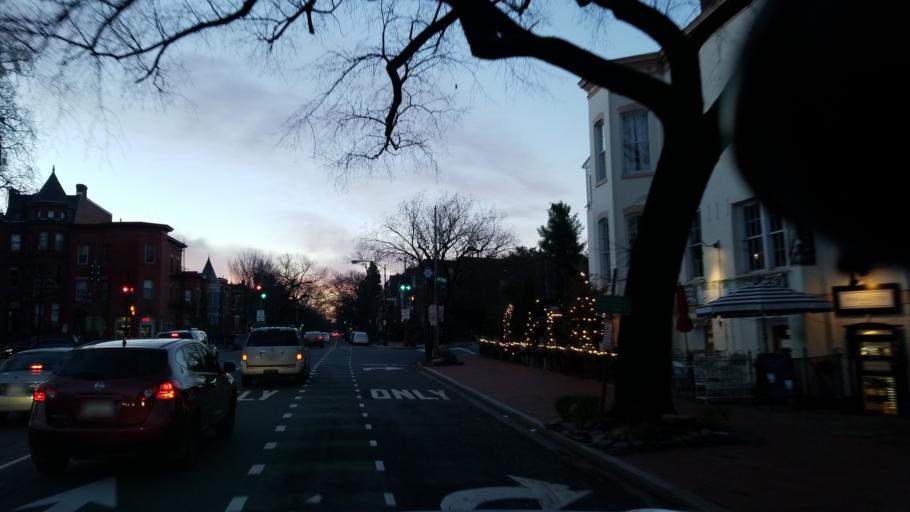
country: US
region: Washington, D.C.
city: Washington, D.C.
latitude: 38.8897
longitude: -76.9916
